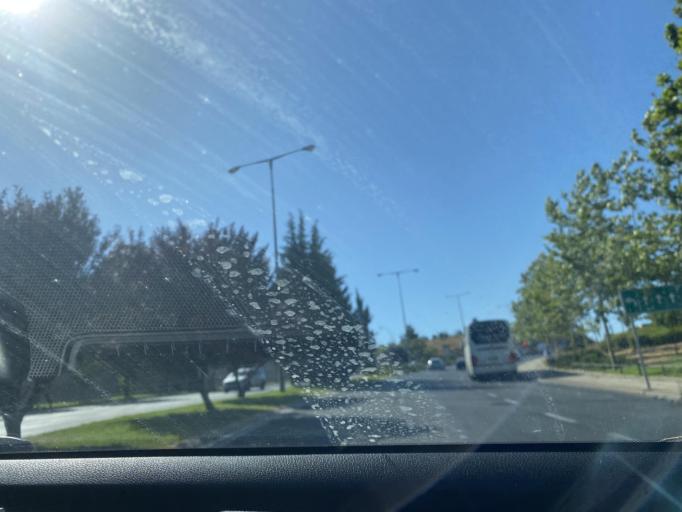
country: PS
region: West Bank
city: Bayt Iksa
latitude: 31.8200
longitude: 35.1911
